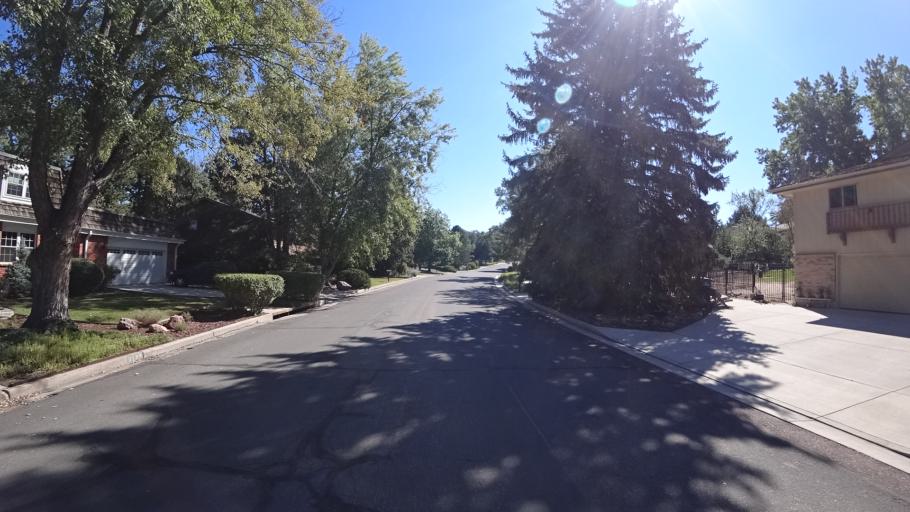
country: US
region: Colorado
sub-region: El Paso County
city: Colorado Springs
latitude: 38.8768
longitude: -104.7836
